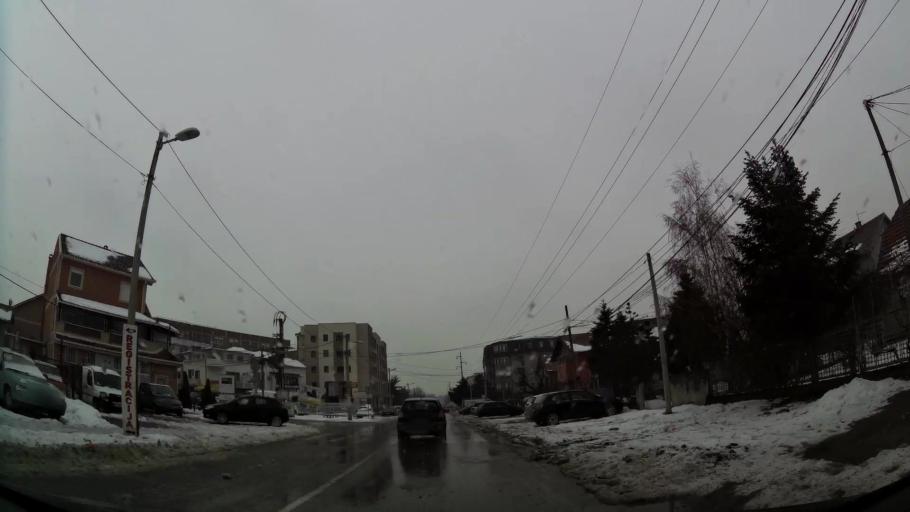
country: RS
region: Central Serbia
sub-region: Belgrade
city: Zemun
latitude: 44.8525
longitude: 20.3639
